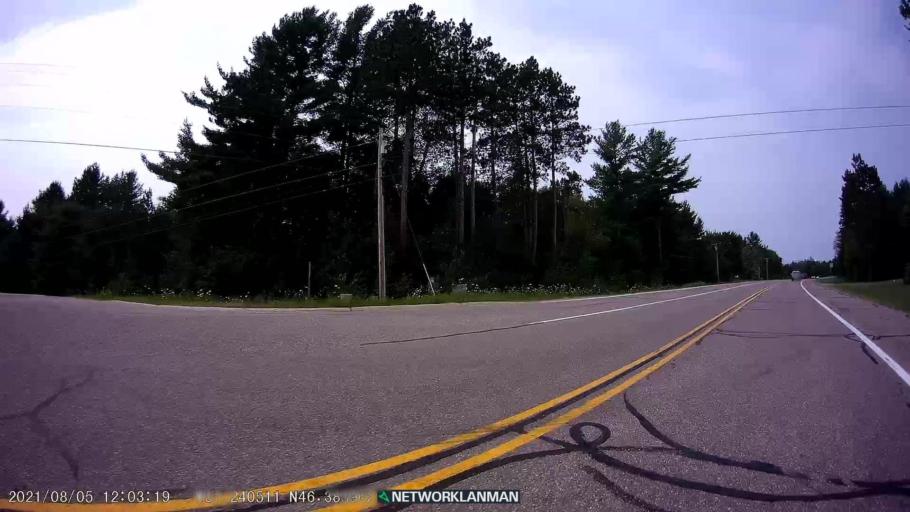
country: US
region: Michigan
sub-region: Marquette County
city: K. I. Sawyer Air Force Base
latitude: 46.3861
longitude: -87.2410
